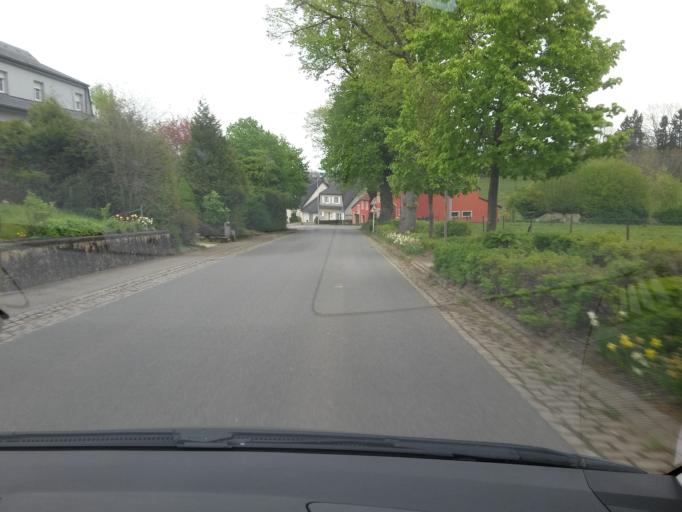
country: LU
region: Luxembourg
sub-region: Canton de Capellen
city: Garnich
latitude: 49.6040
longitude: 5.9282
